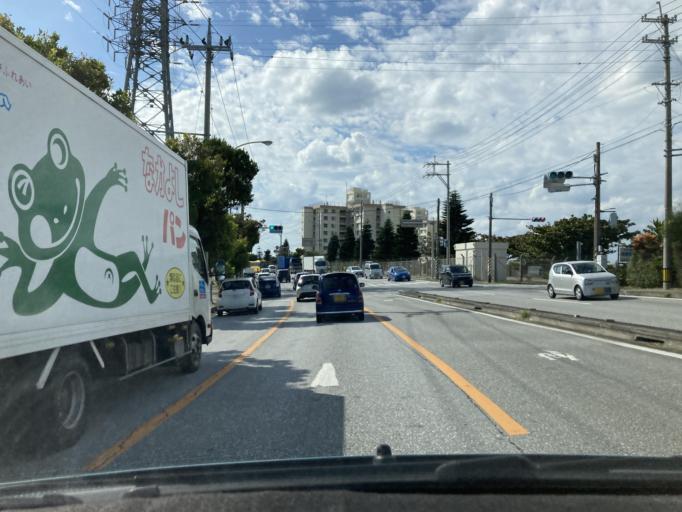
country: JP
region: Okinawa
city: Chatan
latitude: 26.3072
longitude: 127.7776
